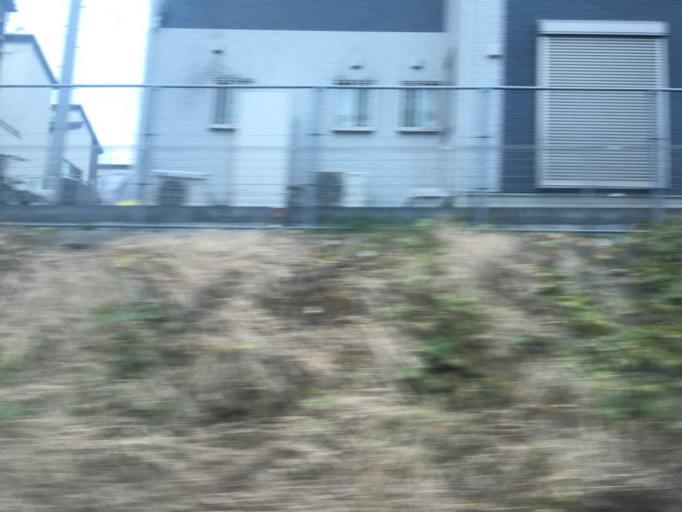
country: JP
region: Saitama
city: Ageoshimo
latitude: 35.9188
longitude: 139.5696
